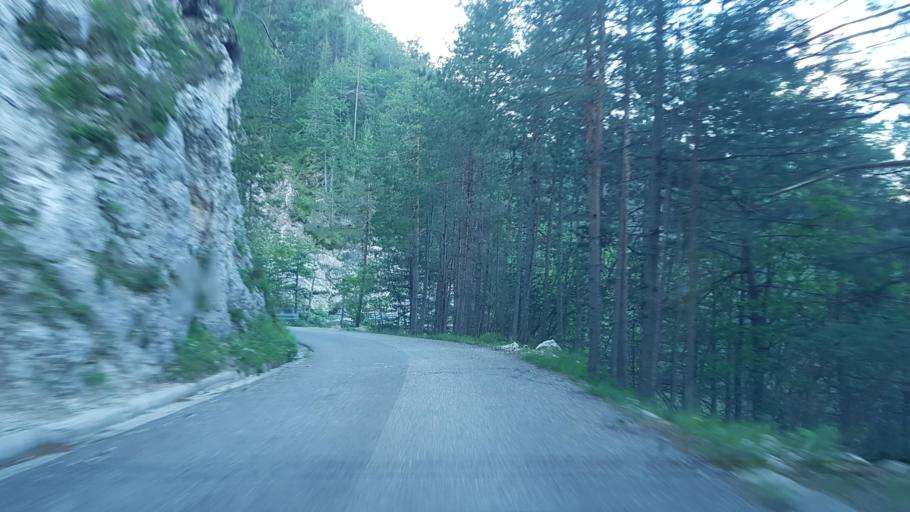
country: IT
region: Friuli Venezia Giulia
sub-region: Provincia di Udine
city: Malborghetto
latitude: 46.4590
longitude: 13.3910
